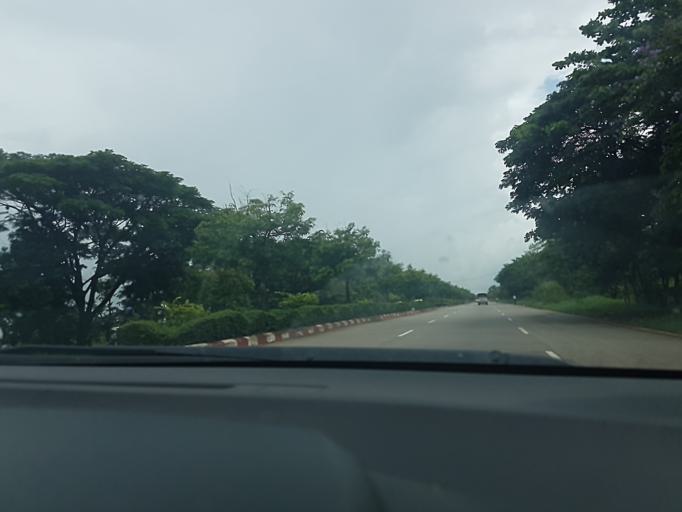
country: MM
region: Bago
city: Thanatpin
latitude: 17.0633
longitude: 96.1628
